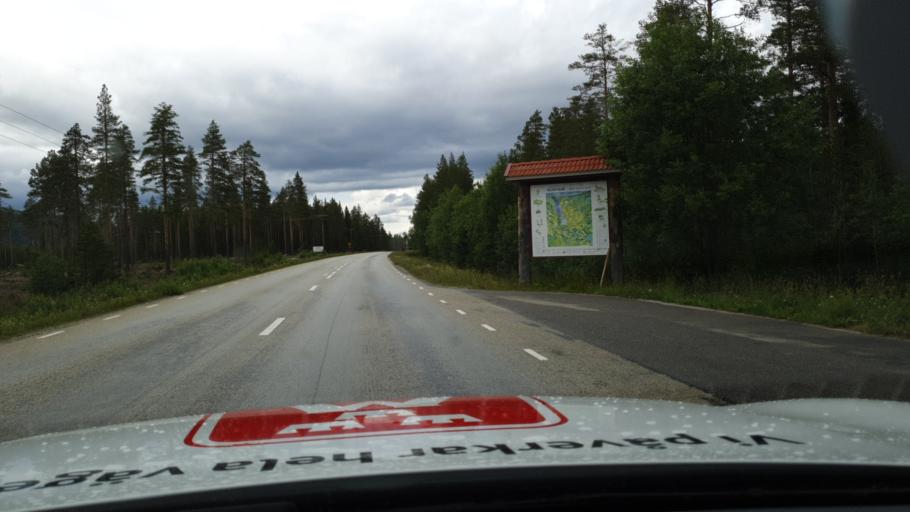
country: SE
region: Jaemtland
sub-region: Bergs Kommun
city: Hoverberg
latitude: 62.5023
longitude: 14.2023
